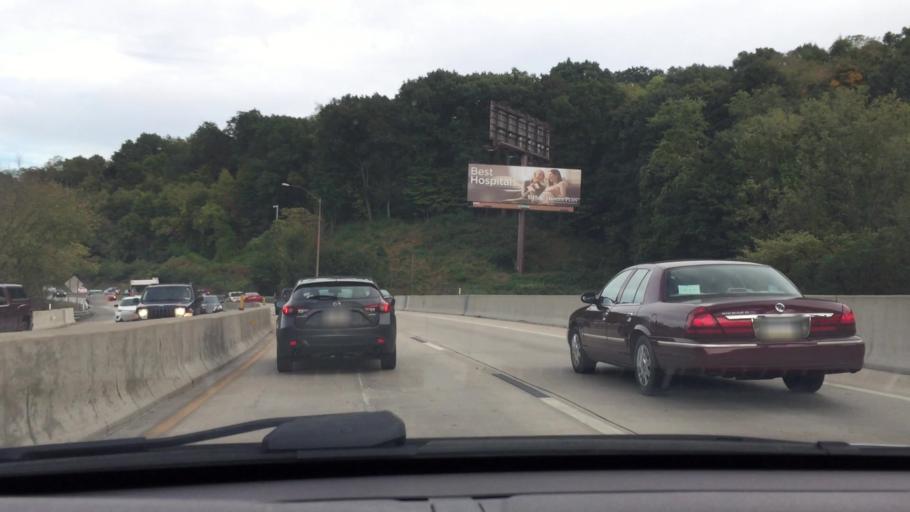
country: US
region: Pennsylvania
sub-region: Allegheny County
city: Carnegie
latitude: 40.4107
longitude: -80.0736
